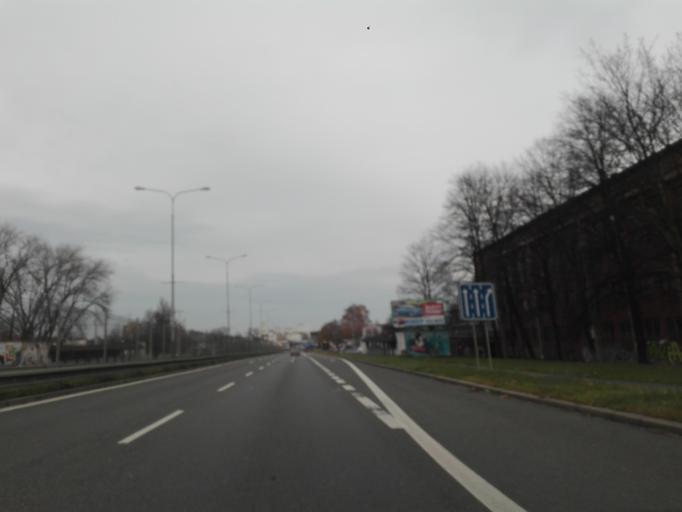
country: CZ
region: Moravskoslezsky
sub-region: Okres Ostrava-Mesto
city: Ostrava
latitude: 49.8219
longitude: 18.2771
